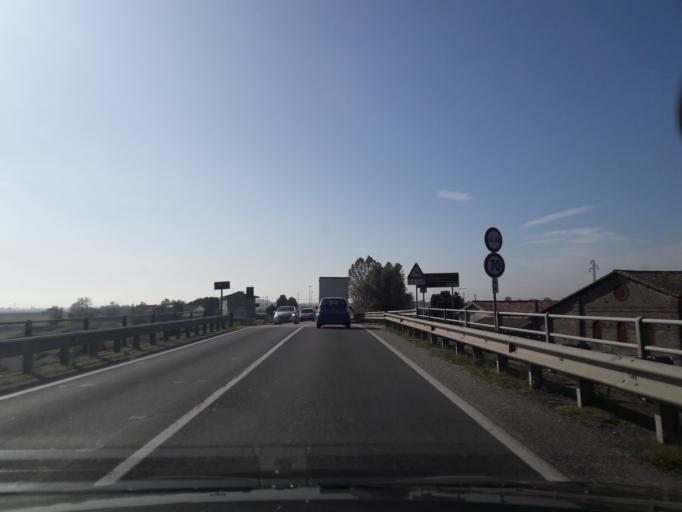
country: IT
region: Veneto
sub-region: Provincia di Rovigo
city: Adria
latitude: 45.0989
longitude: 12.0573
